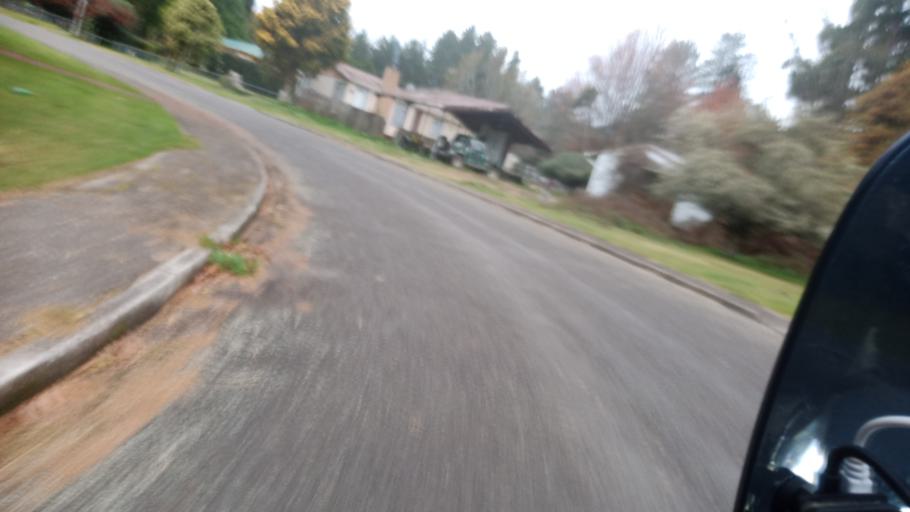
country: NZ
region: Bay of Plenty
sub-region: Whakatane District
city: Murupara
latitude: -38.6455
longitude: 176.7318
